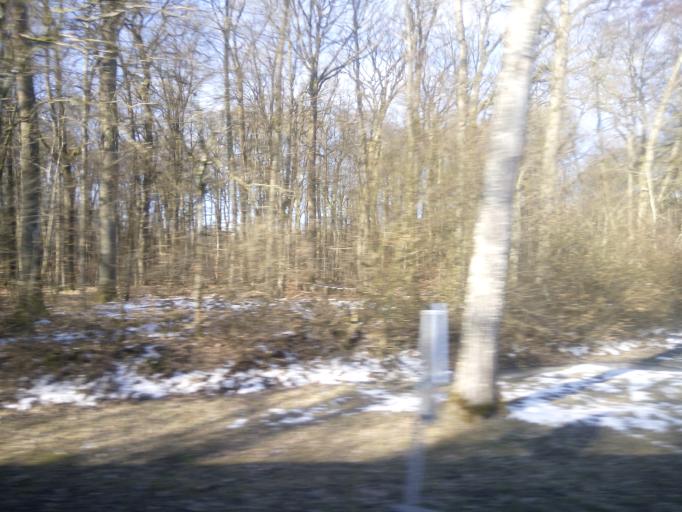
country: LU
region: Grevenmacher
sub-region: Canton d'Echternach
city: Berdorf
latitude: 49.8106
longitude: 6.3408
